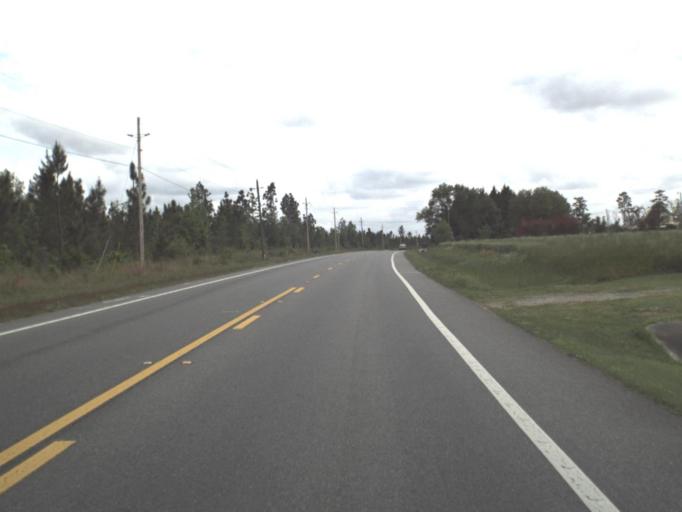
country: US
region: Alabama
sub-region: Escambia County
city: East Brewton
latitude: 30.9287
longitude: -87.0221
